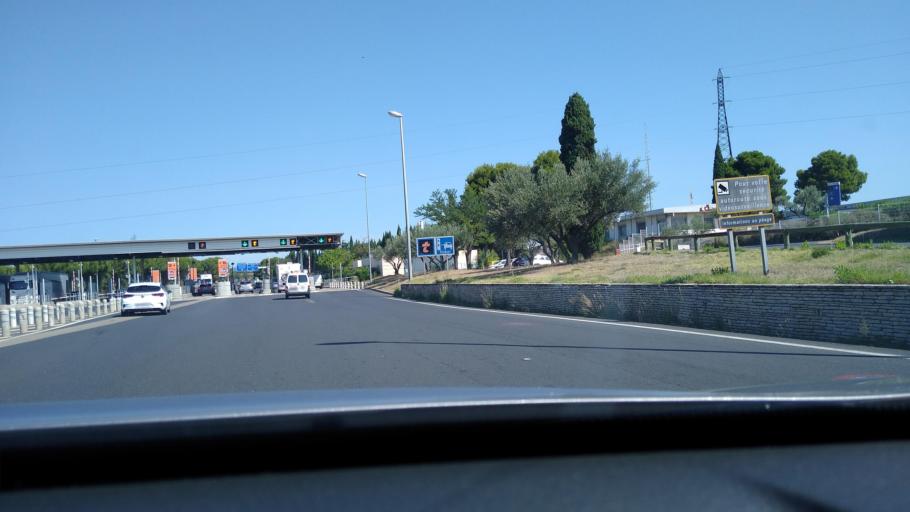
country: FR
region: Languedoc-Roussillon
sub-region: Departement de l'Herault
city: Balaruc-le-Vieux
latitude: 43.4768
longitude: 3.6855
